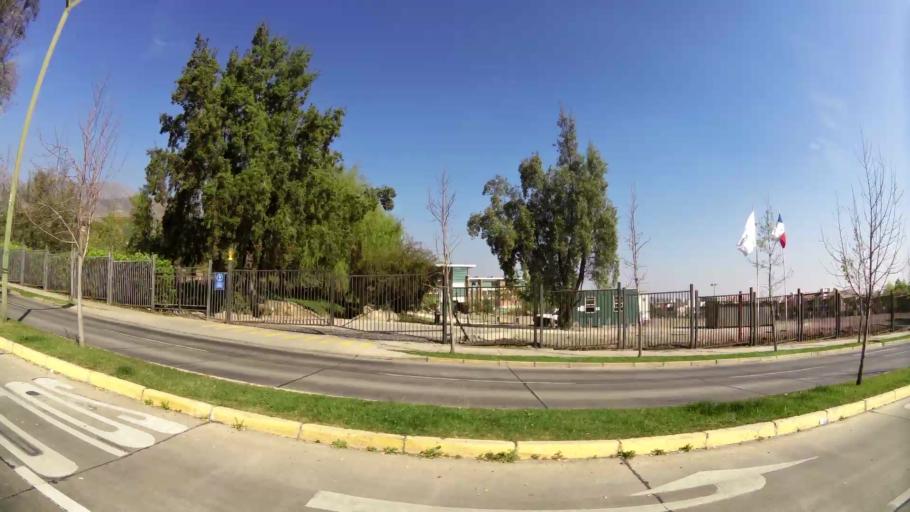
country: CL
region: Santiago Metropolitan
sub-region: Provincia de Santiago
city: Villa Presidente Frei, Nunoa, Santiago, Chile
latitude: -33.4012
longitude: -70.5082
